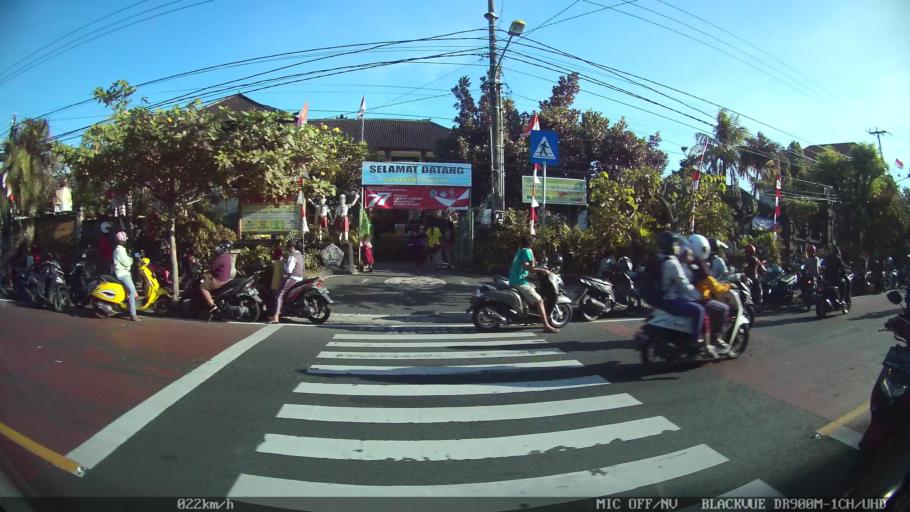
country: ID
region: Bali
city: Banjar Kertasari
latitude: -8.6322
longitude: 115.2024
